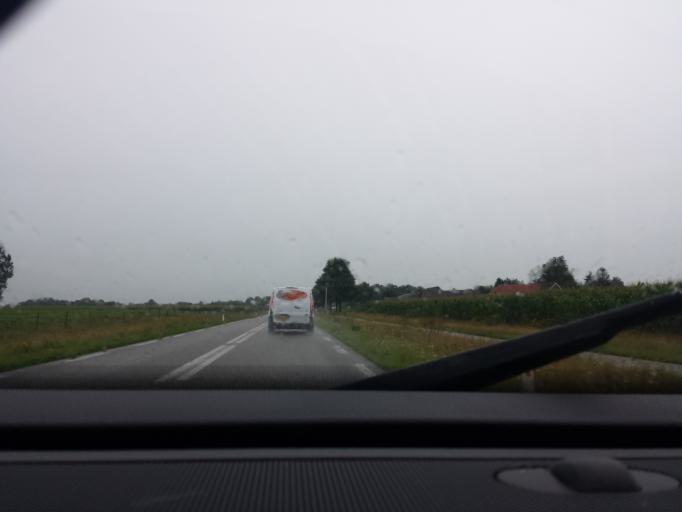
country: NL
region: Gelderland
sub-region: Gemeente Bronckhorst
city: Hengelo
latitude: 52.0260
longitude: 6.3018
